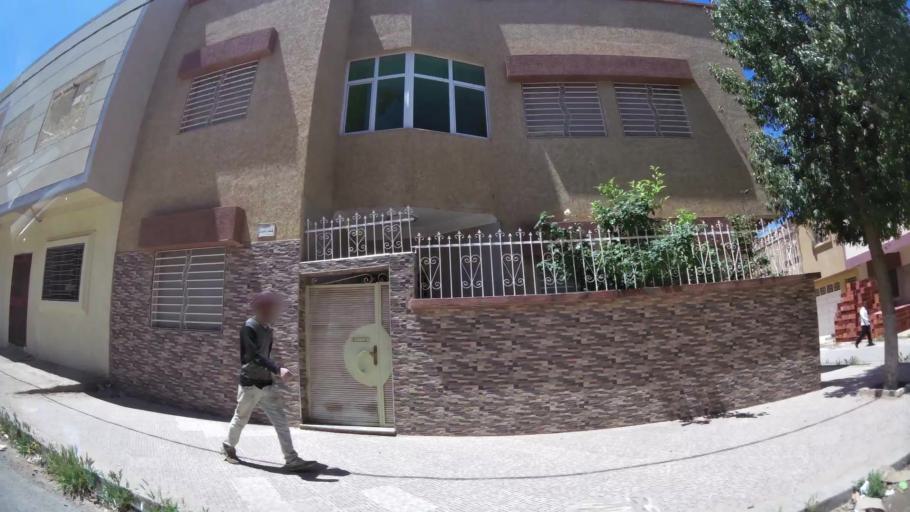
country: MA
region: Oriental
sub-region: Oujda-Angad
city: Oujda
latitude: 34.6578
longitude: -1.9490
